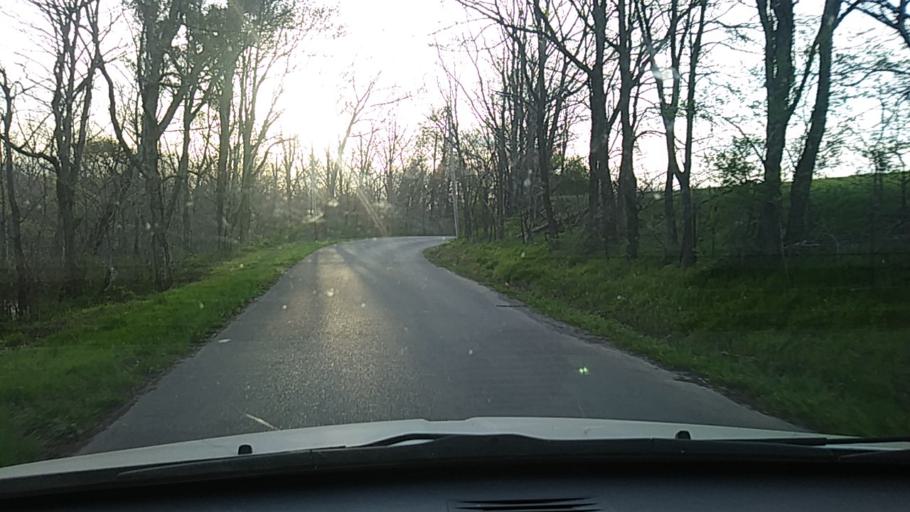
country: US
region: Tennessee
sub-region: Greene County
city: Tusculum
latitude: 36.0936
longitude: -82.7024
